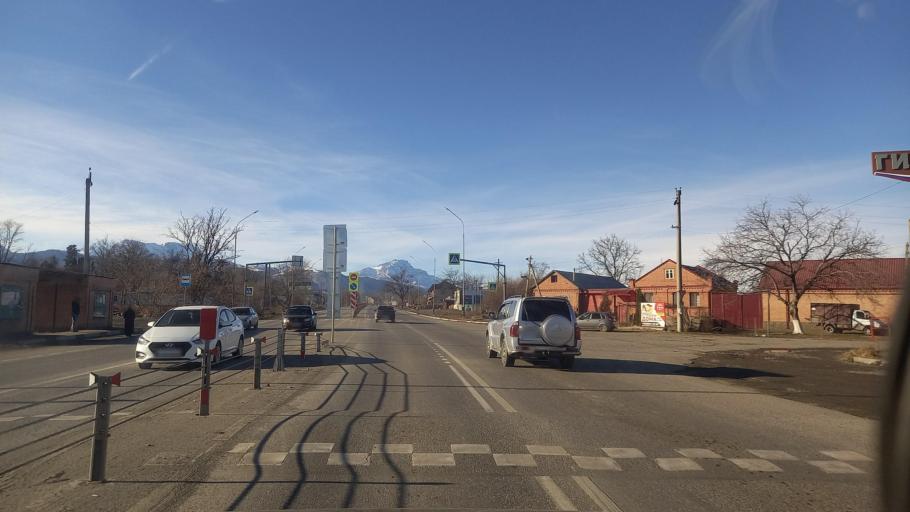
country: RU
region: North Ossetia
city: Gizel'
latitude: 43.0281
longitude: 44.5775
